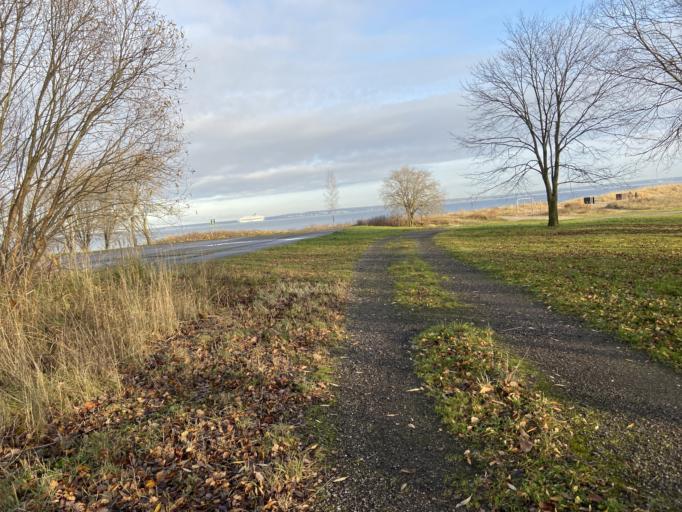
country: EE
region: Harju
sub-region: Tallinna linn
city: Tallinn
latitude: 59.4735
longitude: 24.7218
